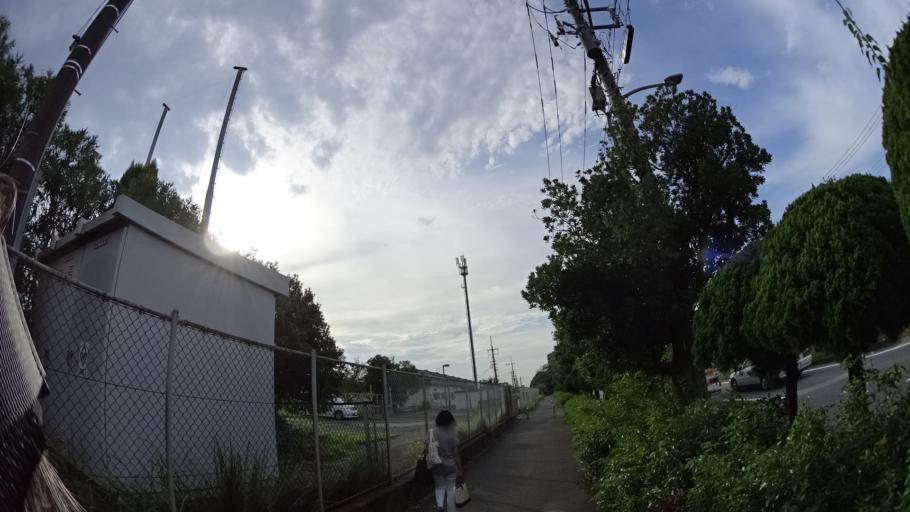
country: JP
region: Chiba
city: Funabashi
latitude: 35.6544
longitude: 140.0350
